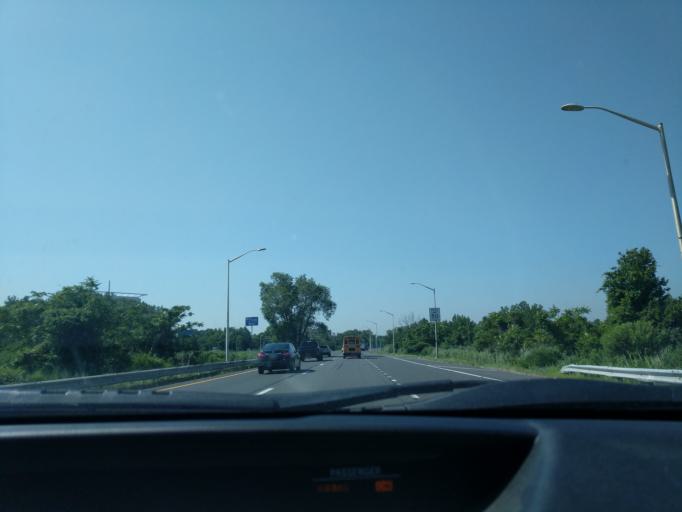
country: US
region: New York
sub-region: Richmond County
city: Bloomfield
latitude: 40.6180
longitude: -74.1776
